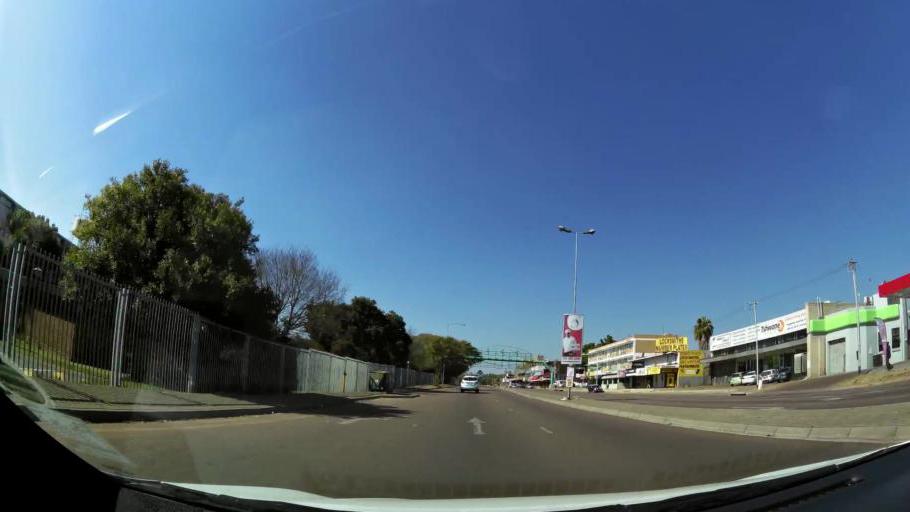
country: ZA
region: Gauteng
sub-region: City of Tshwane Metropolitan Municipality
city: Pretoria
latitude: -25.7600
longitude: 28.2449
